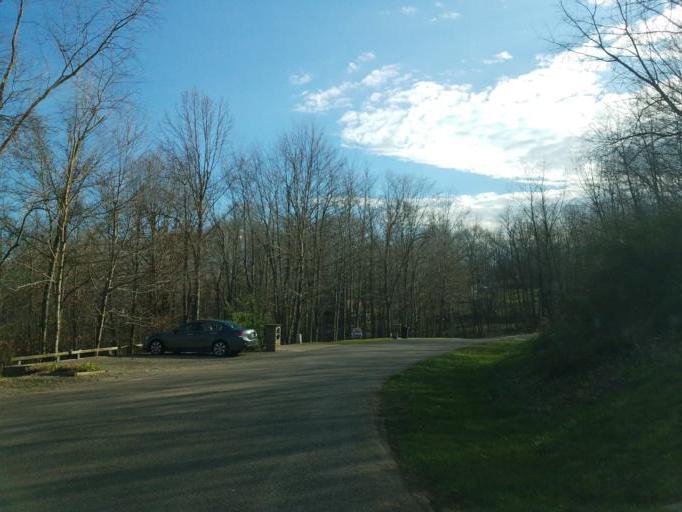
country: US
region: Ohio
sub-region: Knox County
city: Danville
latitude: 40.4514
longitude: -82.3417
